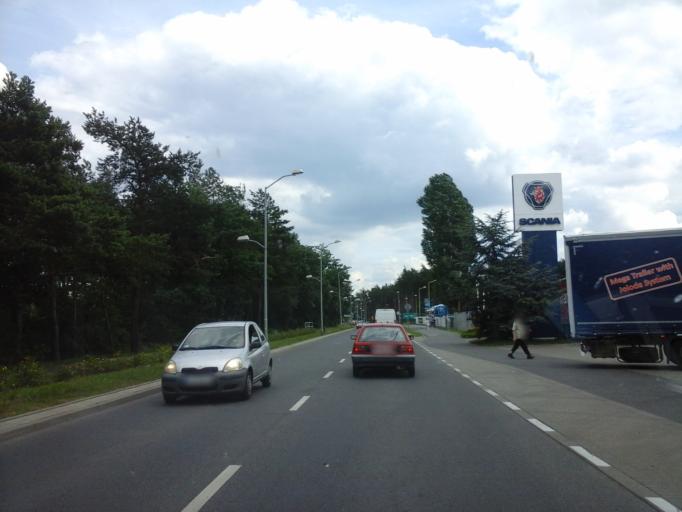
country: PL
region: West Pomeranian Voivodeship
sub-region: Szczecin
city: Szczecin
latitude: 53.3813
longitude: 14.6783
